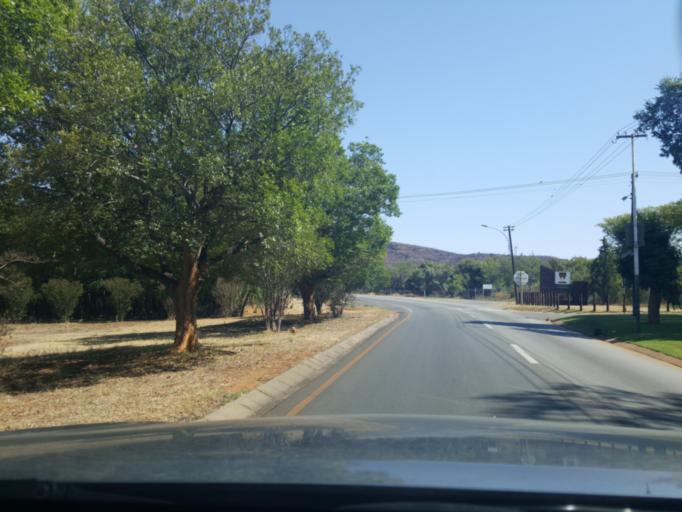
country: ZA
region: North-West
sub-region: Ngaka Modiri Molema District Municipality
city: Zeerust
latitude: -25.5261
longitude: 26.0747
